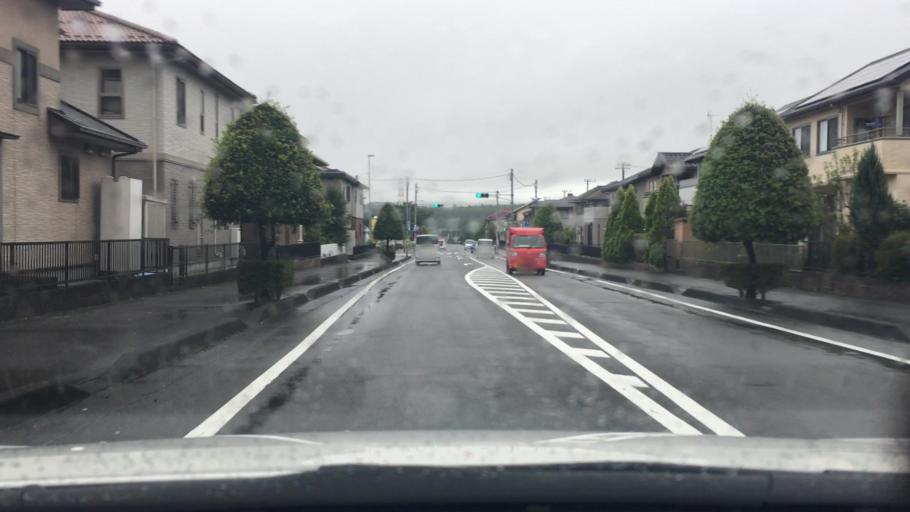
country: JP
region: Shizuoka
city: Gotemba
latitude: 35.2390
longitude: 138.9155
